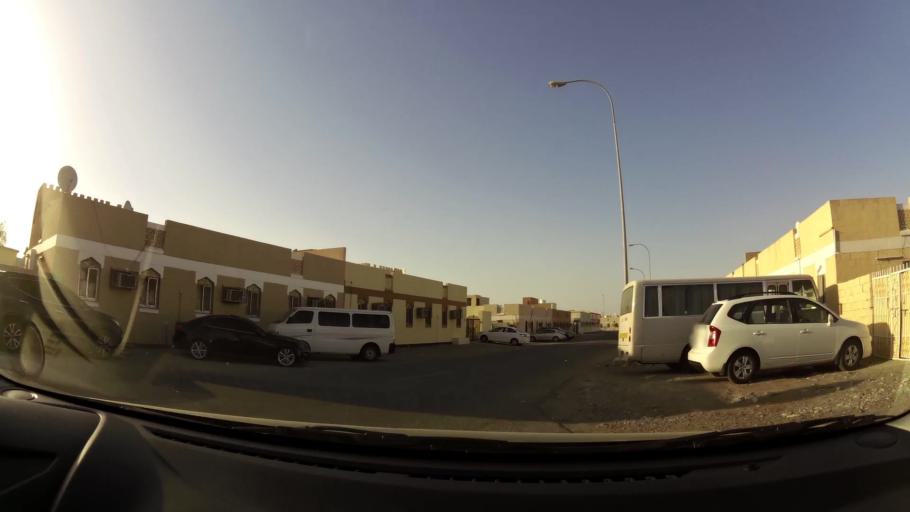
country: OM
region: Muhafazat Masqat
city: As Sib al Jadidah
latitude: 23.6261
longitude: 58.1925
